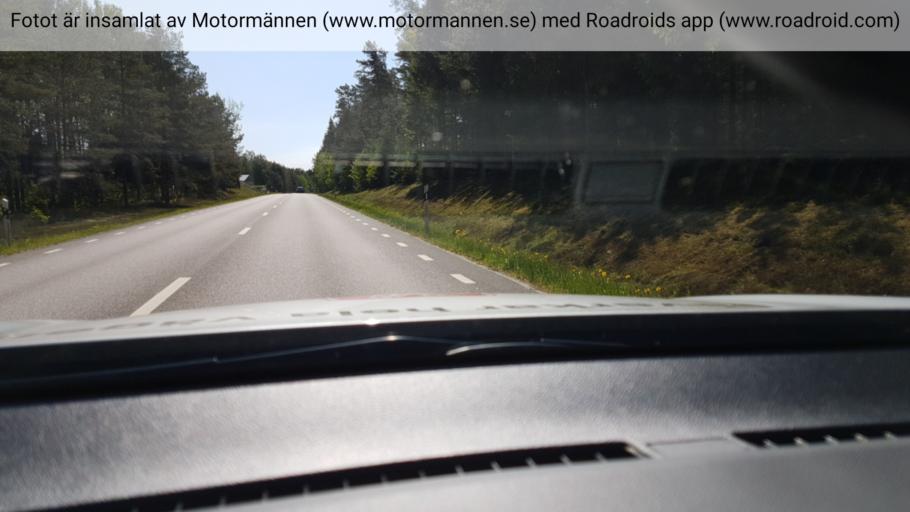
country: SE
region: Vaestra Goetaland
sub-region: Hjo Kommun
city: Hjo
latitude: 58.3373
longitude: 14.2393
